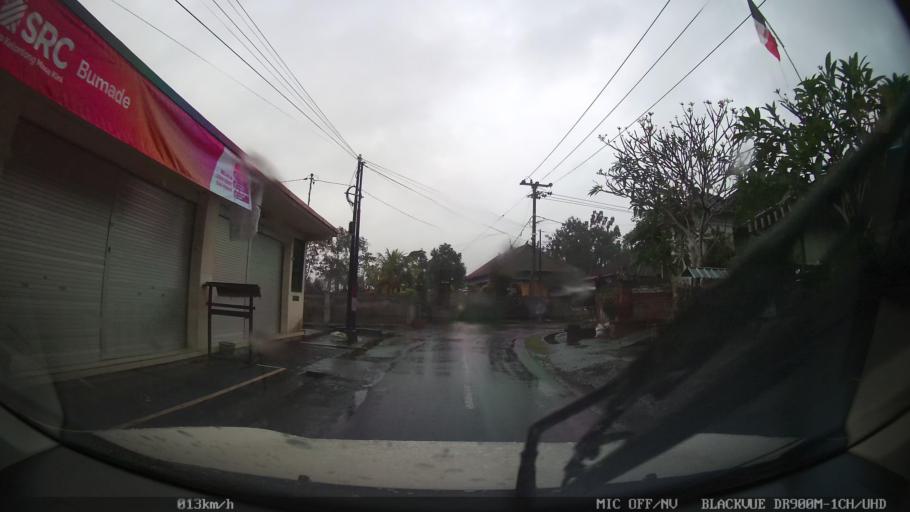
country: ID
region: Bali
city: Banjar Sedang
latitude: -8.5662
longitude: 115.2531
